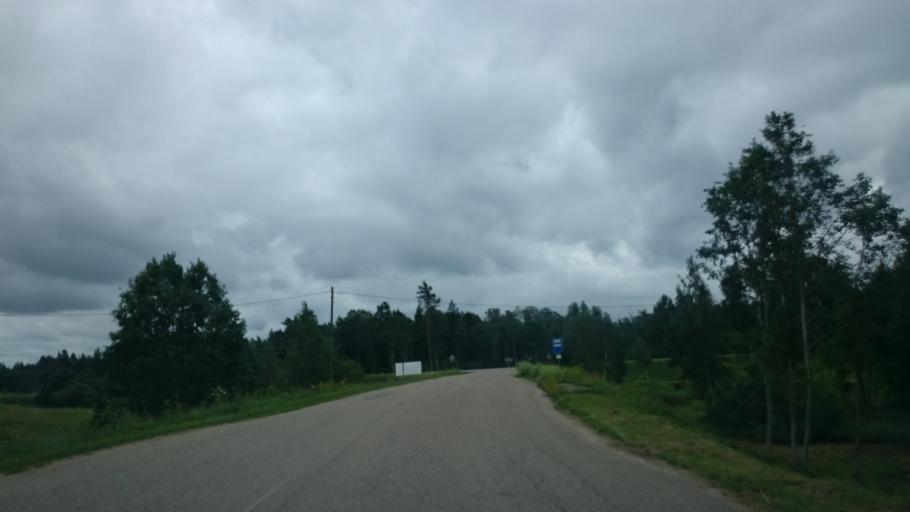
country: LV
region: Aizpute
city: Aizpute
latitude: 56.7116
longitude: 21.4813
